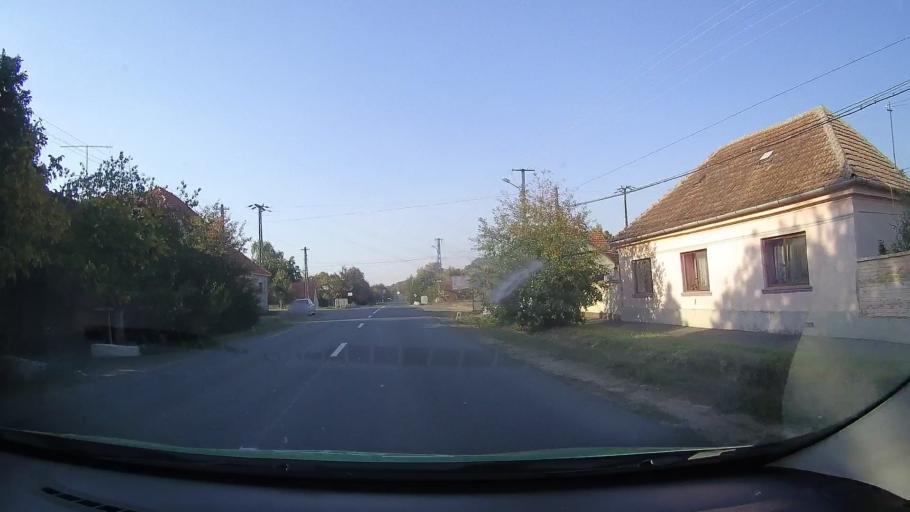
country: RO
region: Arad
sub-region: Comuna Ghioroc
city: Ghioroc
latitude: 46.1393
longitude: 21.6037
